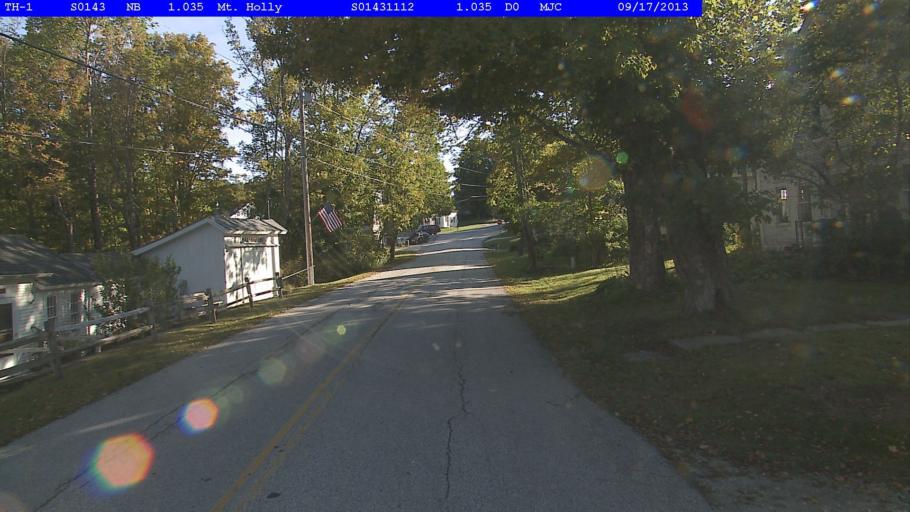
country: US
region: Vermont
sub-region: Rutland County
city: Rutland
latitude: 43.4143
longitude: -72.8221
